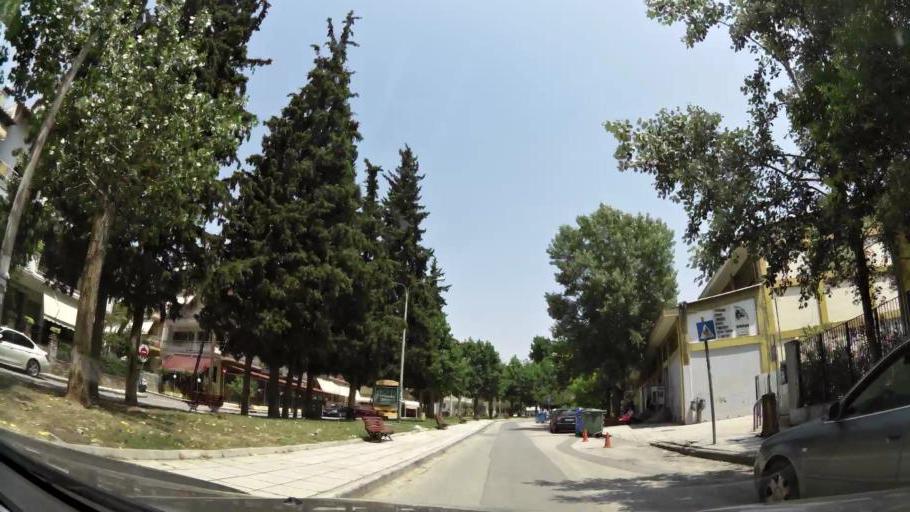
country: GR
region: Central Macedonia
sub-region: Nomos Thessalonikis
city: Evosmos
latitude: 40.6674
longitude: 22.9006
